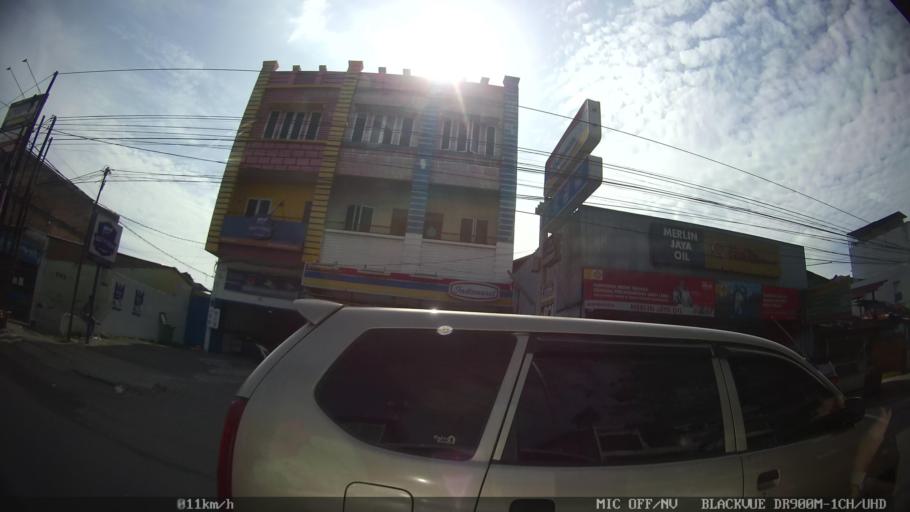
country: ID
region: North Sumatra
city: Medan
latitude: 3.5742
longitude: 98.6429
